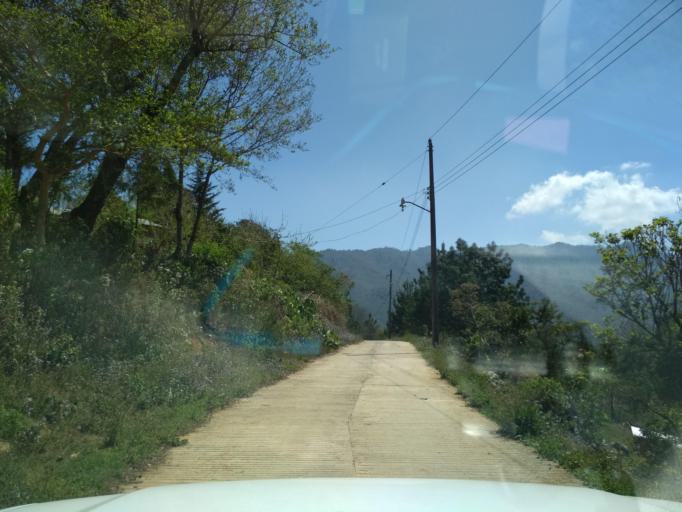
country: MX
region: Veracruz
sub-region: Tlilapan
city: Tonalixco
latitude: 18.7749
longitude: -97.0887
